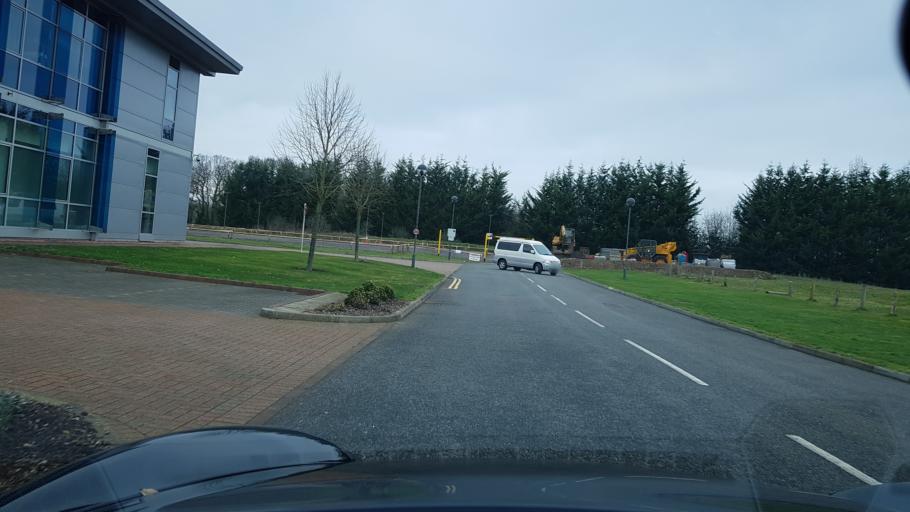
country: GB
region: England
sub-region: Surrey
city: Guildford
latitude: 51.2425
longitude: -0.6178
